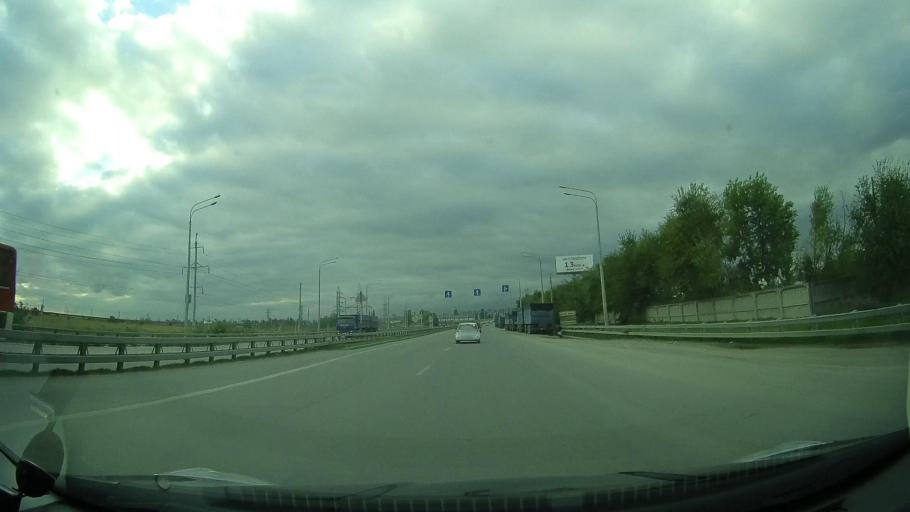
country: RU
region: Rostov
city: Rostov-na-Donu
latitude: 47.2024
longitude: 39.7189
